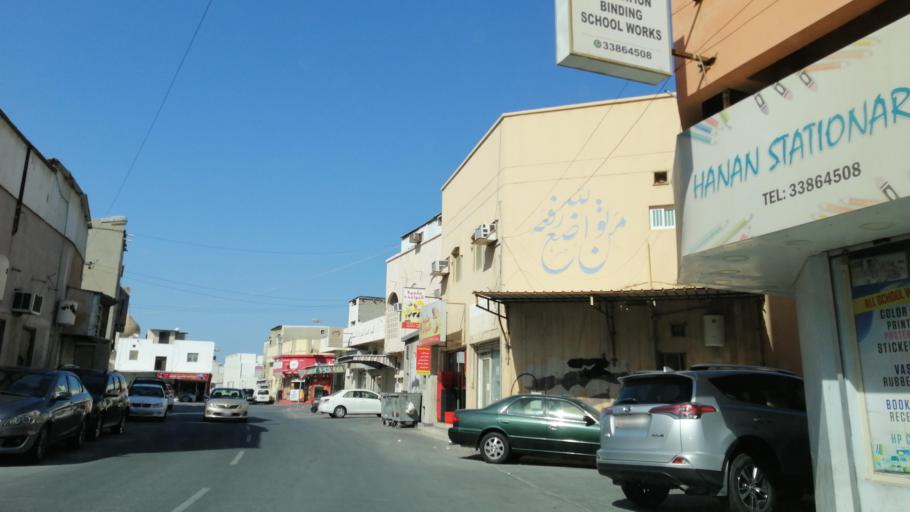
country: BH
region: Muharraq
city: Al Muharraq
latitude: 26.2519
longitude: 50.6327
